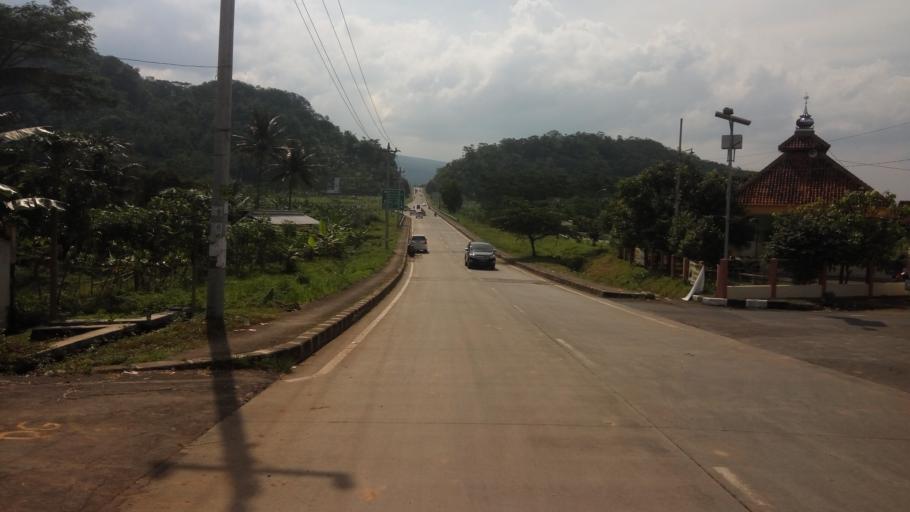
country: ID
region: Central Java
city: Ungaran
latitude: -7.1351
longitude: 110.4213
